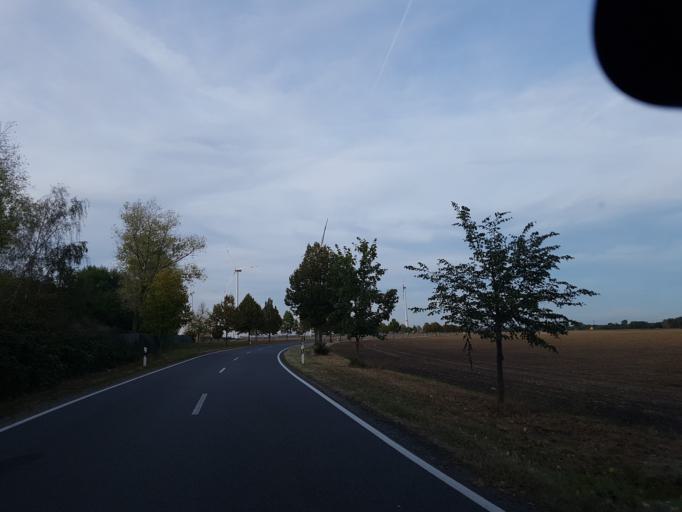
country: DE
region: Saxony
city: Glaubitz
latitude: 51.3320
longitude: 13.3749
